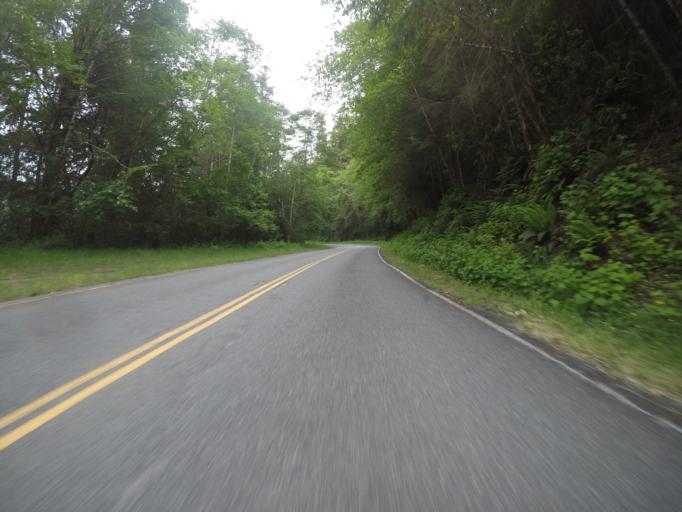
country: US
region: California
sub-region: Del Norte County
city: Bertsch-Oceanview
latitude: 41.7680
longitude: -124.0104
